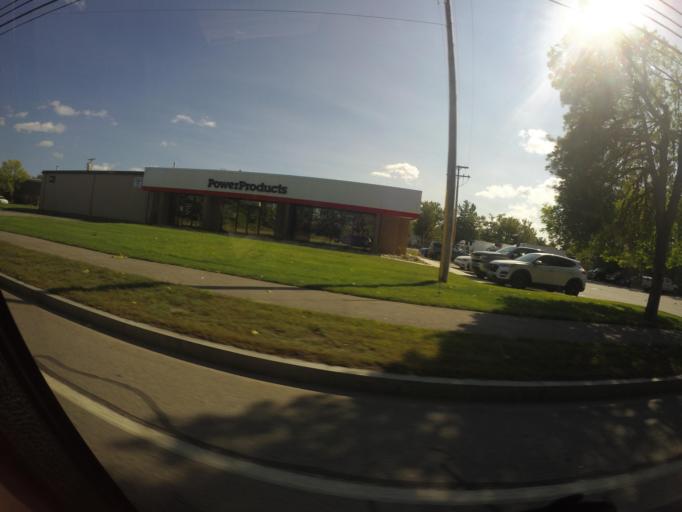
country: US
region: Maine
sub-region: Cumberland County
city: South Portland Gardens
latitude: 43.6869
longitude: -70.3169
